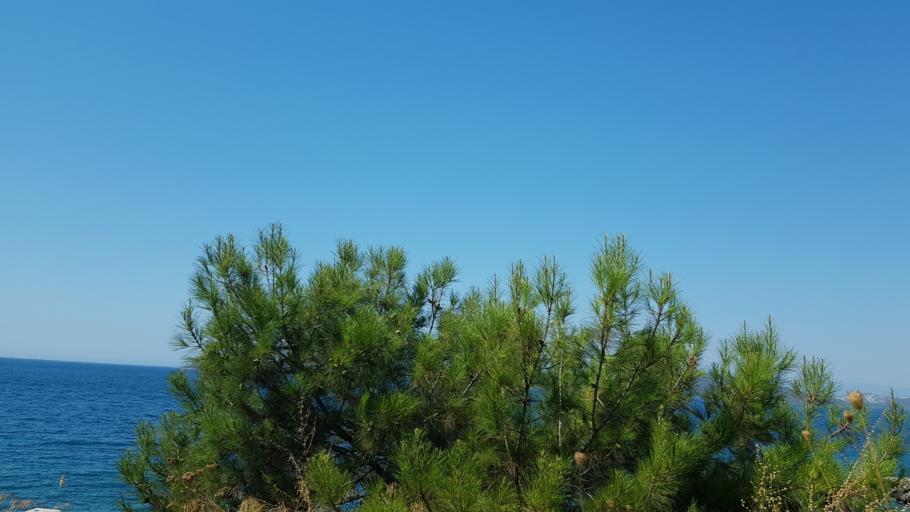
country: TR
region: Mugla
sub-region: Bodrum
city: Bodrum
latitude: 37.1091
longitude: 27.5133
